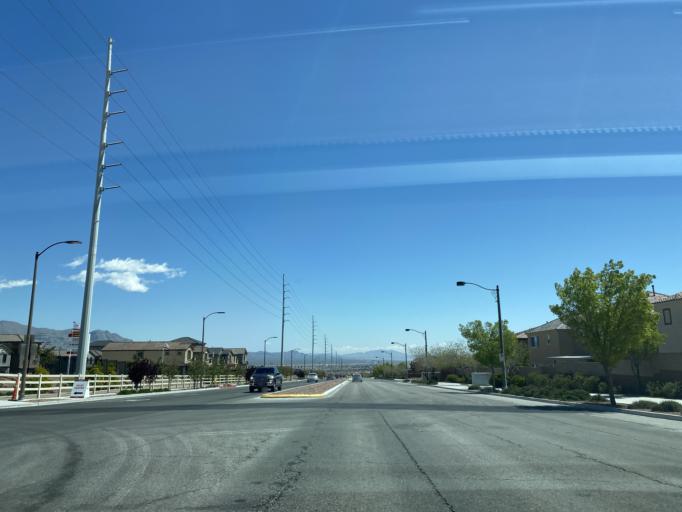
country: US
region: Nevada
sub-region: Clark County
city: Summerlin South
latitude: 36.3058
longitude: -115.3269
